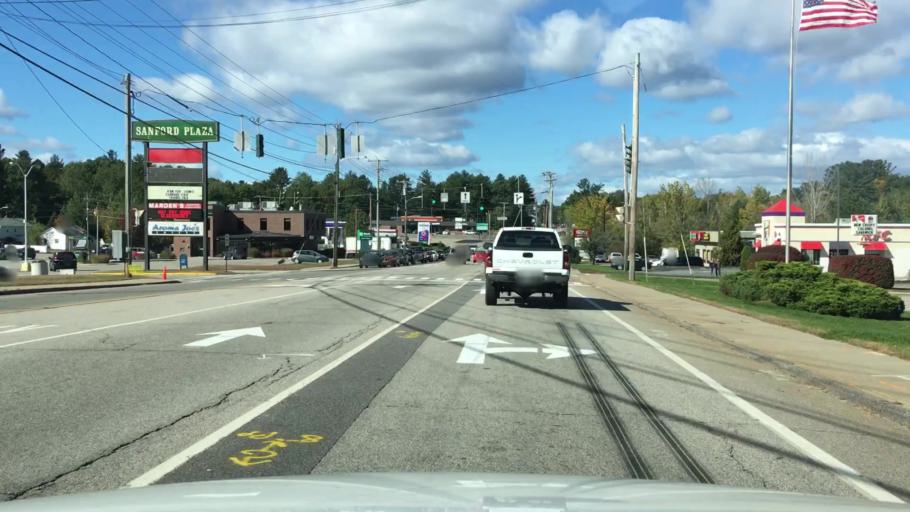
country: US
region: Maine
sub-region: York County
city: South Sanford
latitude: 43.4189
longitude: -70.7555
